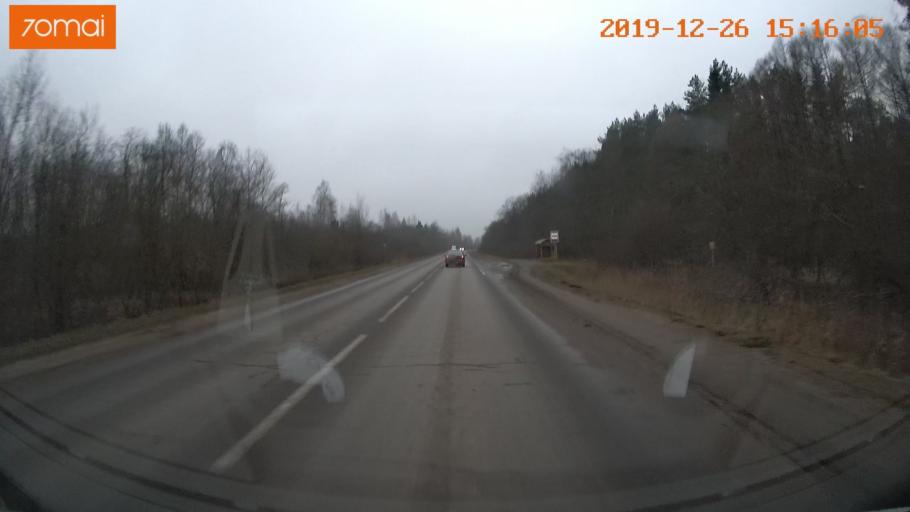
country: RU
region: Jaroslavl
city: Rybinsk
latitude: 58.0902
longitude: 38.8707
